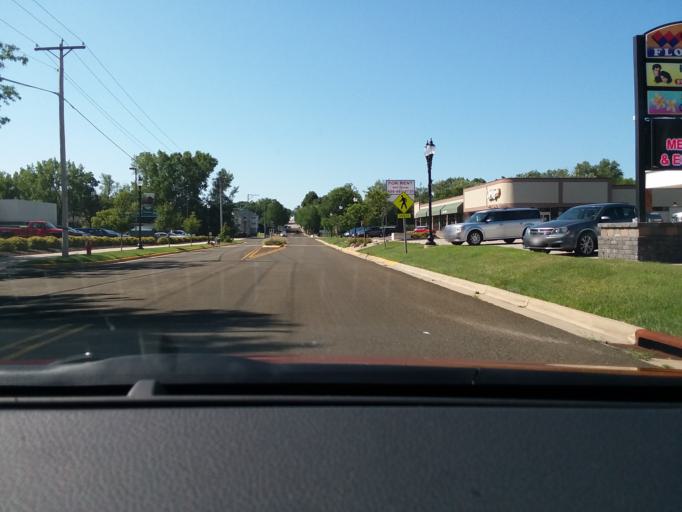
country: US
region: Wisconsin
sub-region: Dane County
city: De Forest
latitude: 43.2511
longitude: -89.3440
